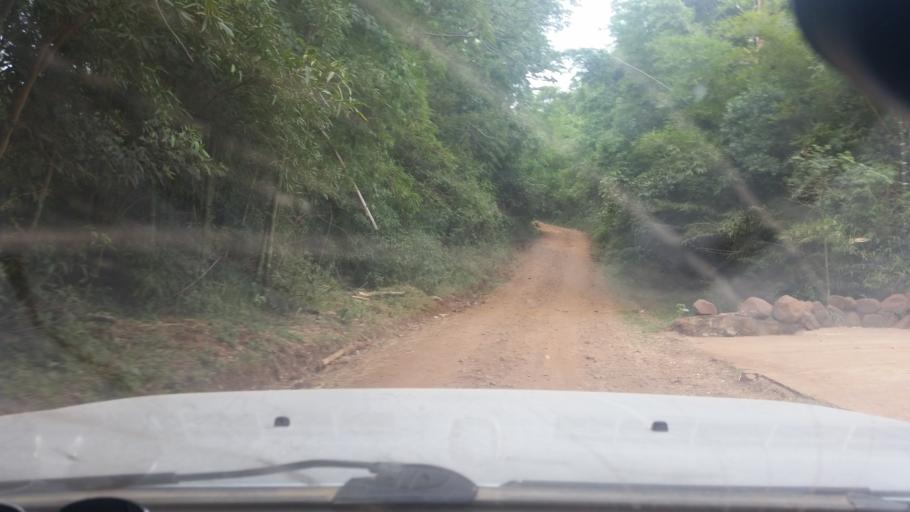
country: PY
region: Guaira
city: Independencia
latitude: -25.8057
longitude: -56.2727
